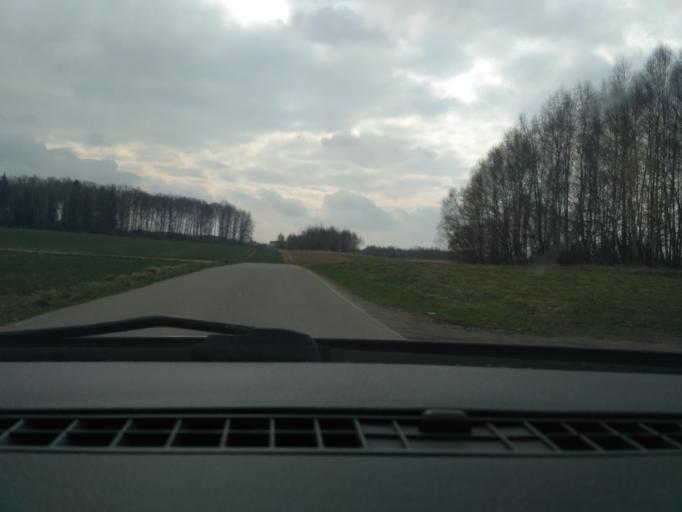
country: PL
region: Subcarpathian Voivodeship
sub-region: Powiat krosnienski
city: Kroscienko Wyzne
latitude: 49.6707
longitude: 21.8278
